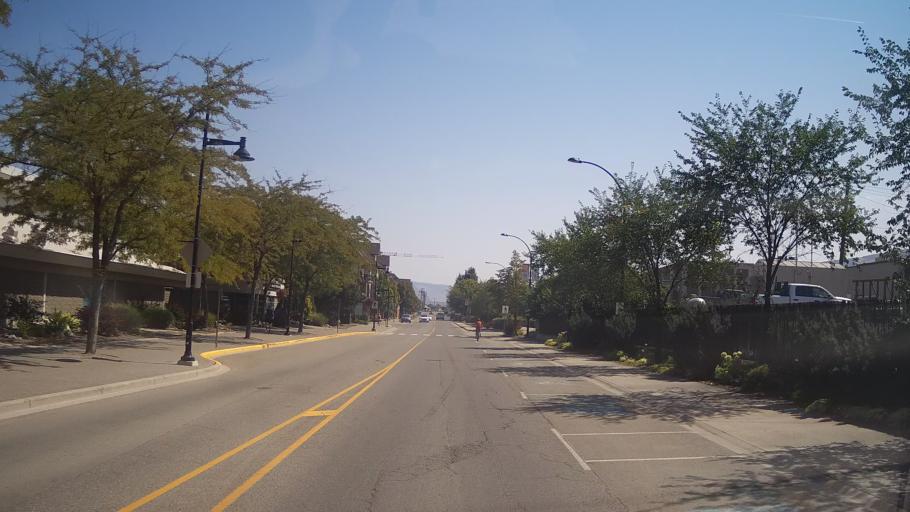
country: CA
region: British Columbia
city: Kamloops
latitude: 50.6781
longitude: -120.3334
